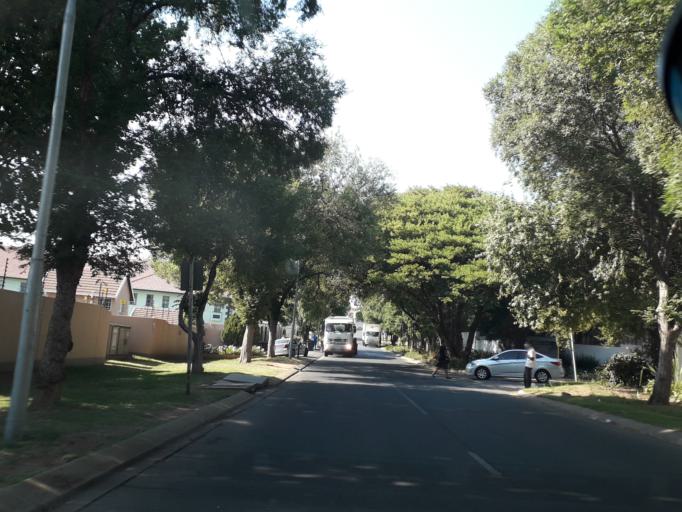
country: ZA
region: Gauteng
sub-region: City of Johannesburg Metropolitan Municipality
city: Midrand
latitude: -26.0345
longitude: 28.0582
